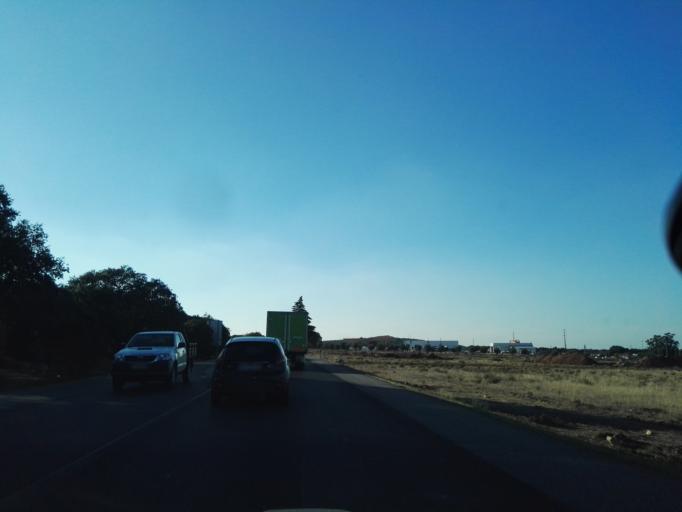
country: PT
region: Evora
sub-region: Borba
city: Borba
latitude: 38.8238
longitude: -7.5056
